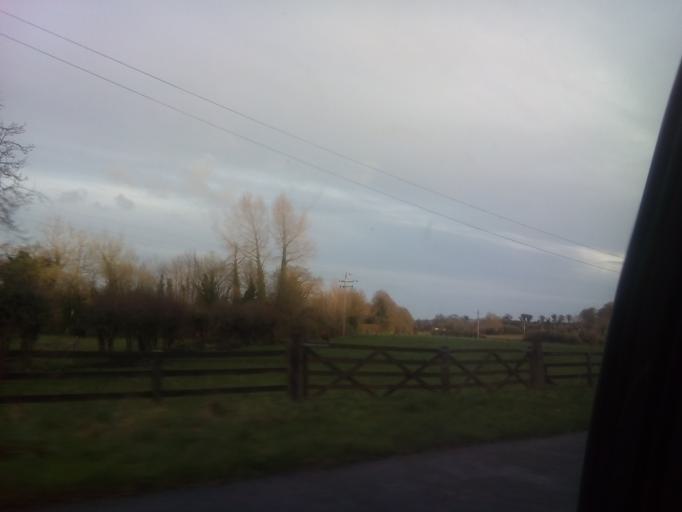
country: IE
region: Leinster
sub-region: Laois
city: Abbeyleix
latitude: 52.8858
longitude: -7.3643
